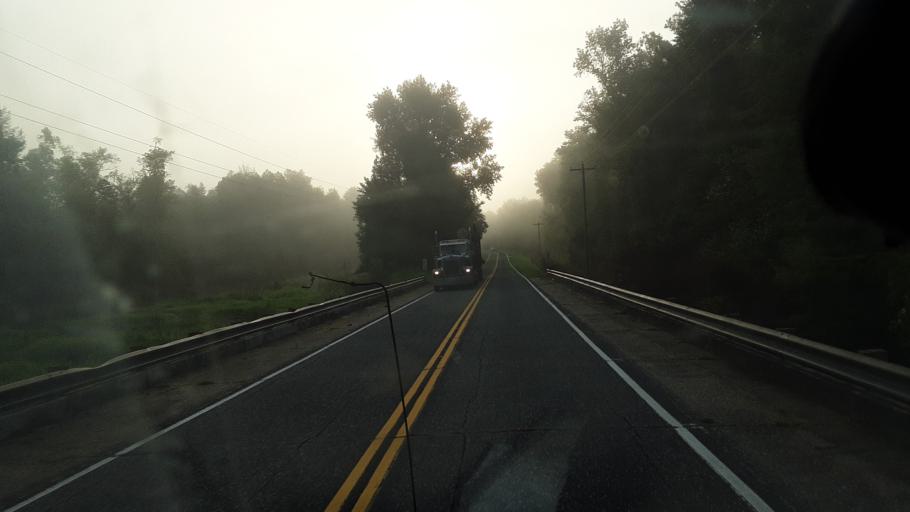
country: US
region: South Carolina
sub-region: Williamsburg County
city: Kingstree
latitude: 33.8236
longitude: -79.9571
